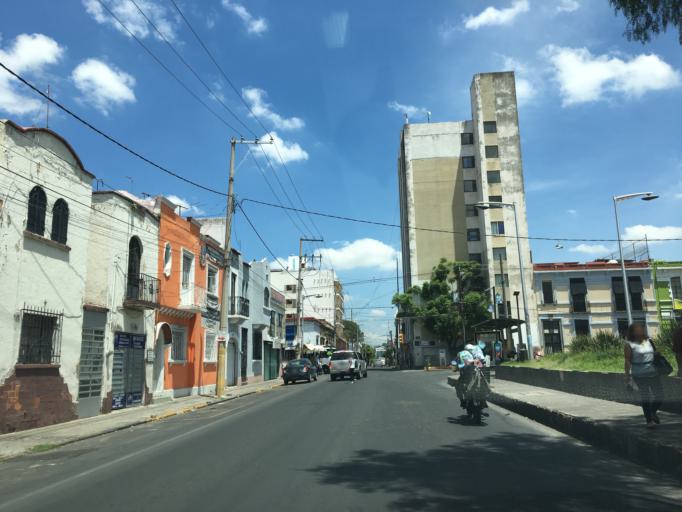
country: MX
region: Puebla
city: Puebla
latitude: 19.0448
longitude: -98.2090
